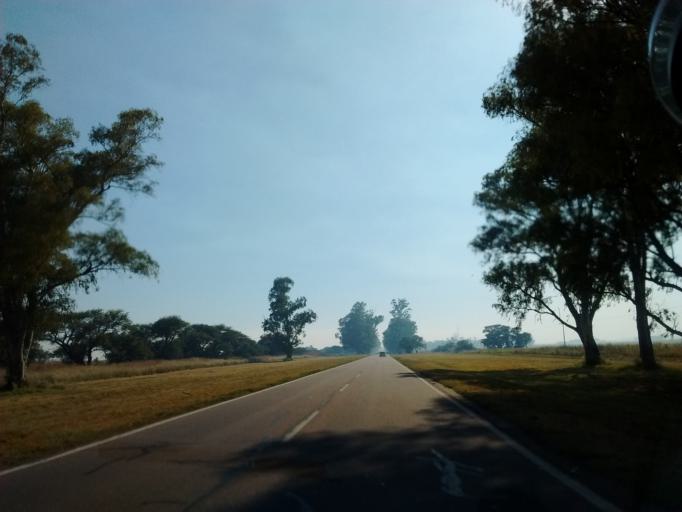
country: AR
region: La Pampa
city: Anguil
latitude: -36.5706
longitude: -64.1444
